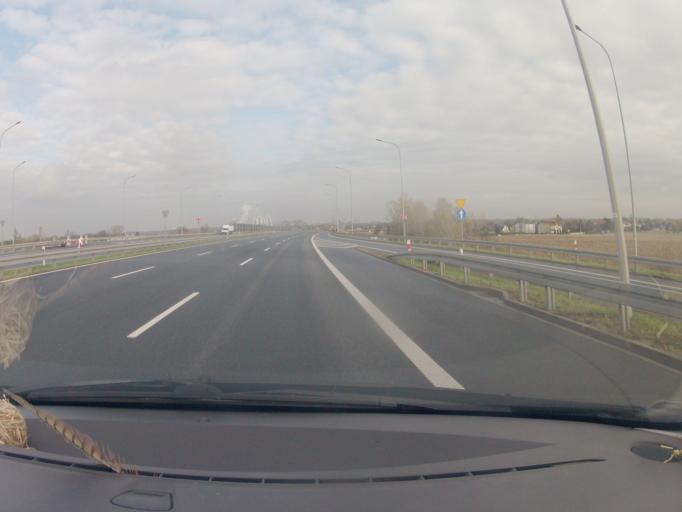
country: PL
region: Lesser Poland Voivodeship
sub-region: Powiat wielicki
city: Kokotow
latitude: 50.0395
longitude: 20.0656
